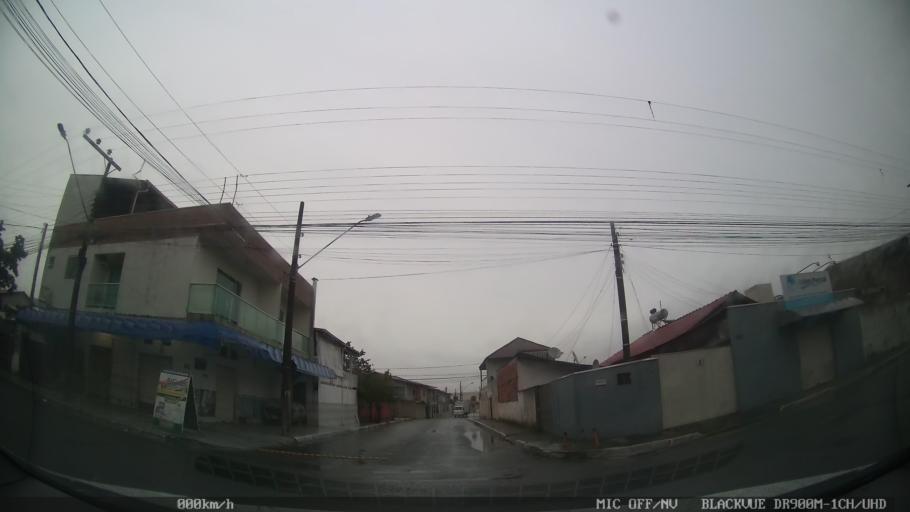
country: BR
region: Santa Catarina
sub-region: Itajai
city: Itajai
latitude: -26.9248
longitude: -48.6924
